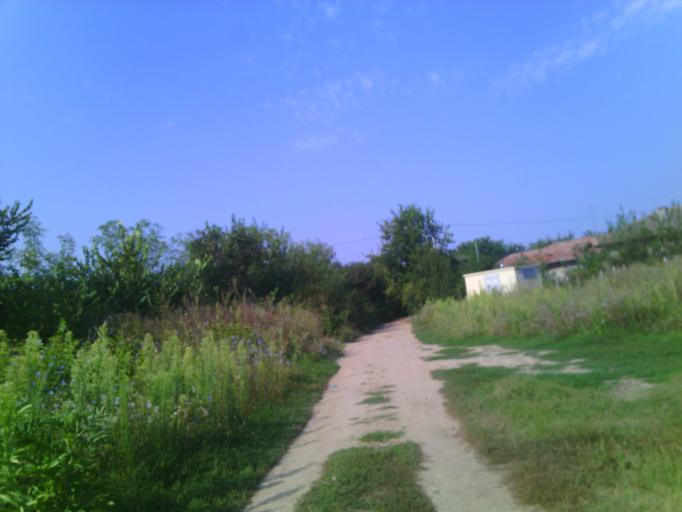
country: RO
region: Giurgiu
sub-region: Comuna Valea Dragului
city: Valea Dragului
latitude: 44.2057
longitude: 26.2724
